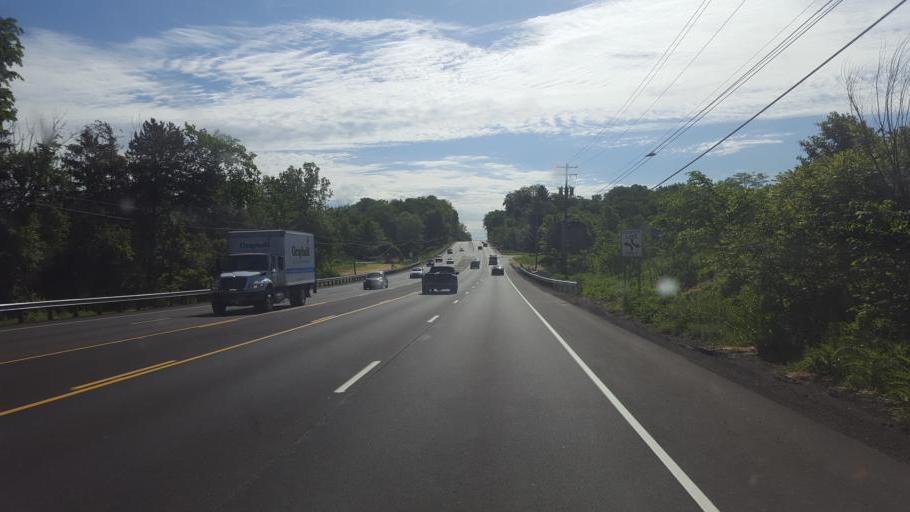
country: US
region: Ohio
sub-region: Summit County
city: Montrose-Ghent
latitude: 41.1357
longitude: -81.6780
